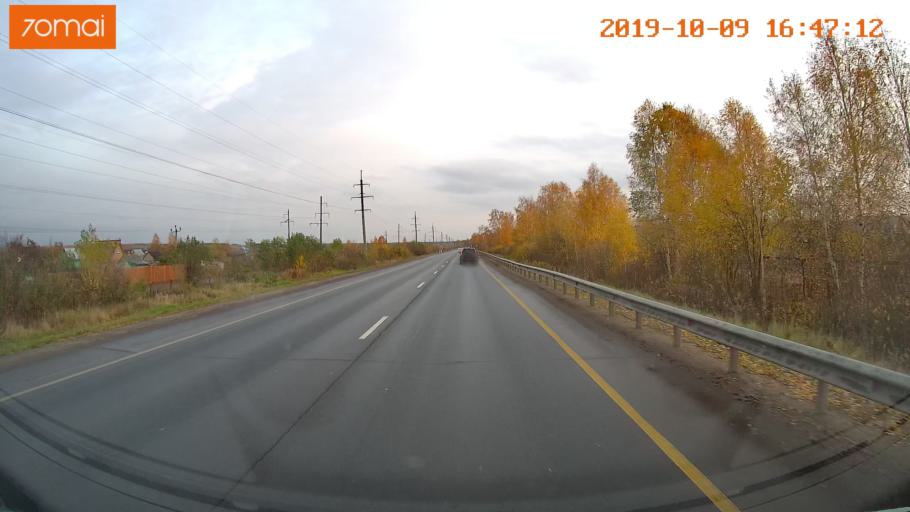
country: RU
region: Kostroma
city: Volgorechensk
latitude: 57.4386
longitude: 41.1744
